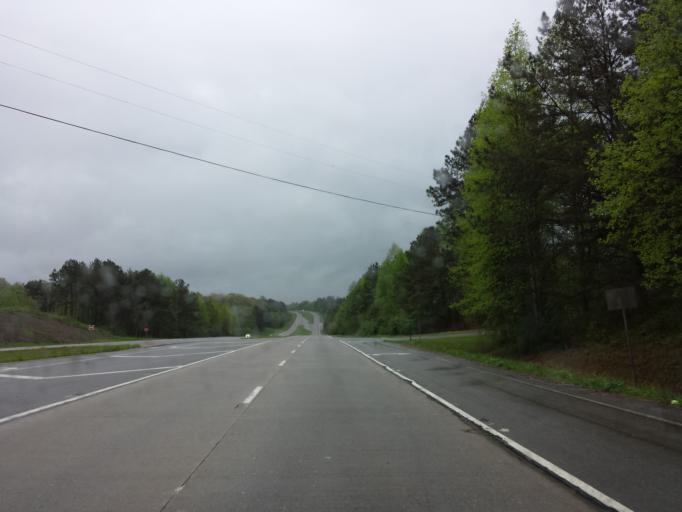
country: US
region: Georgia
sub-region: Pickens County
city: Jasper
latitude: 34.4221
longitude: -84.4310
